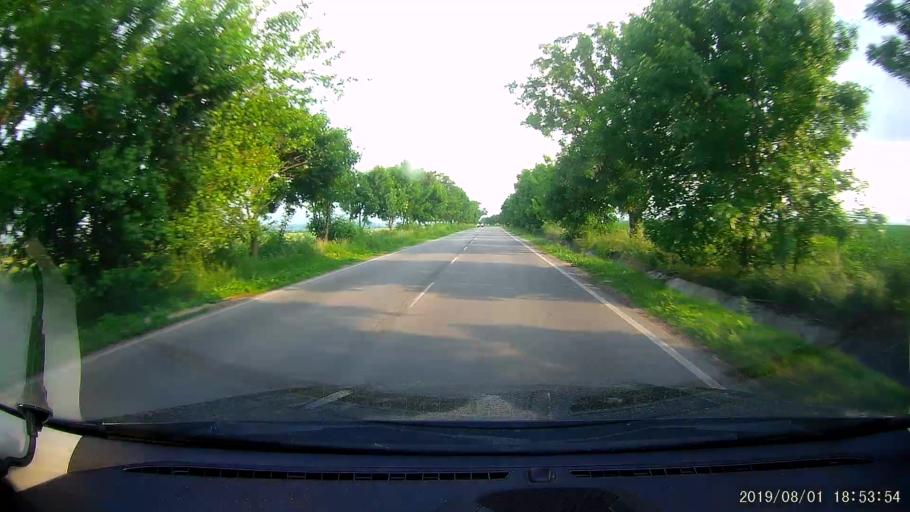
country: BG
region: Shumen
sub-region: Obshtina Shumen
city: Shumen
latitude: 43.2121
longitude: 26.9983
